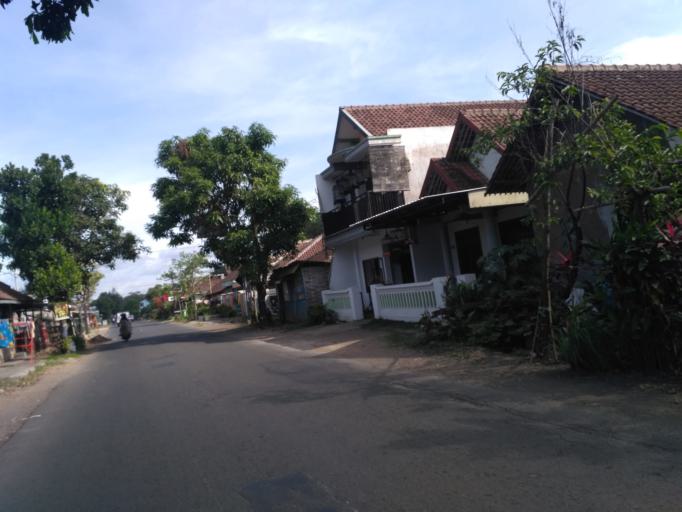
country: ID
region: East Java
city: Golek
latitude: -8.0642
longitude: 112.6266
